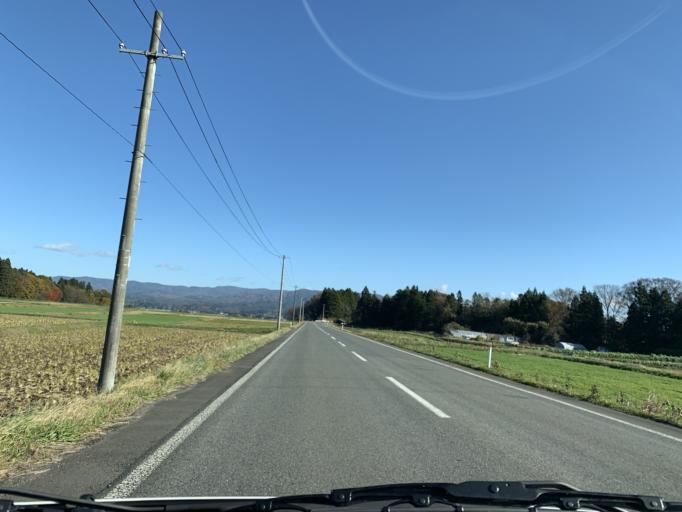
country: JP
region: Iwate
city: Mizusawa
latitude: 39.0949
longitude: 141.1242
